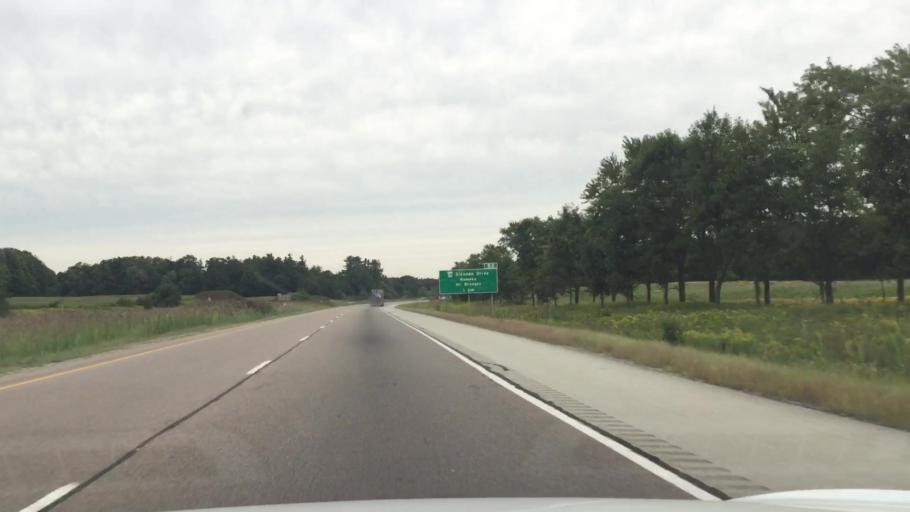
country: CA
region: Ontario
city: Delaware
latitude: 42.9139
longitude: -81.4553
